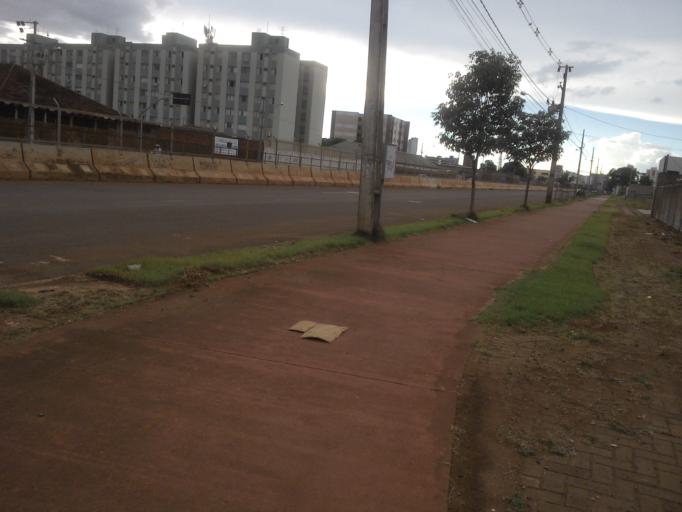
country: BR
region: Parana
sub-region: Maringa
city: Maringa
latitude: -23.4235
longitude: -51.9145
